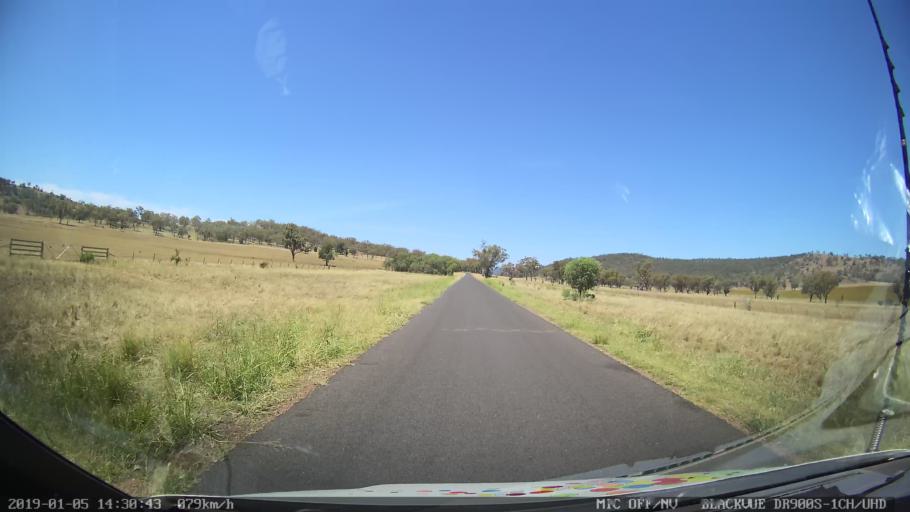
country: AU
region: New South Wales
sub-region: Tamworth Municipality
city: Phillip
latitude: -31.2277
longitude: 150.5964
